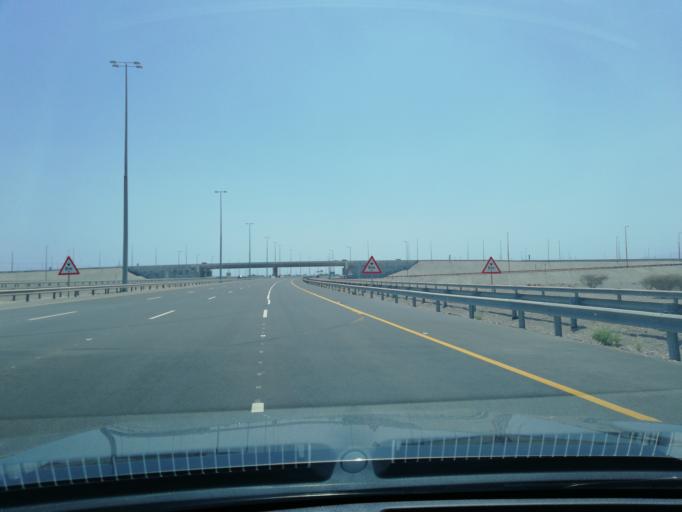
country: OM
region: Al Batinah
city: Barka'
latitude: 23.6330
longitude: 57.8694
